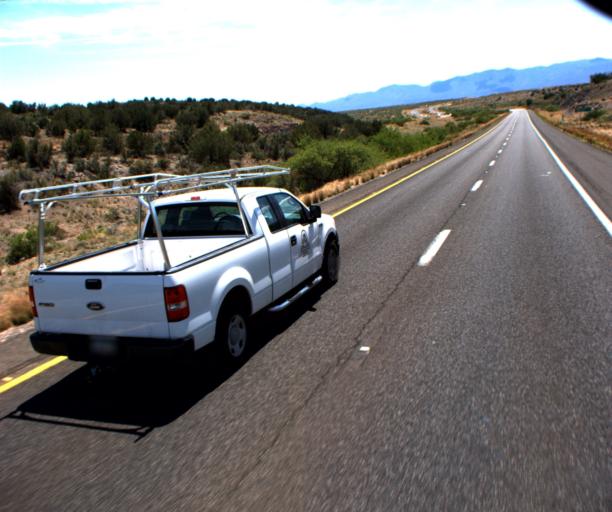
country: US
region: Arizona
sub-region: Yavapai County
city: Cornville
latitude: 34.7875
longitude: -111.9212
